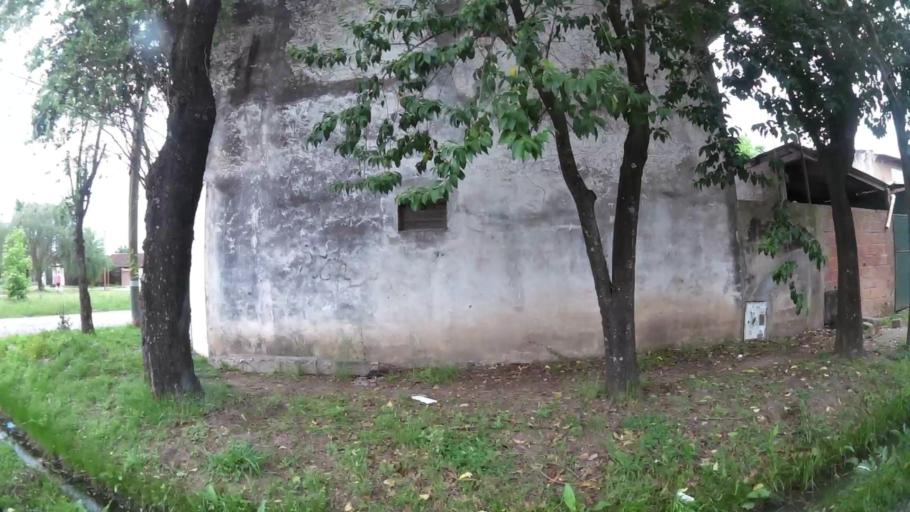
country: AR
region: Buenos Aires
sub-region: Partido de Campana
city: Campana
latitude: -34.1951
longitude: -58.9468
